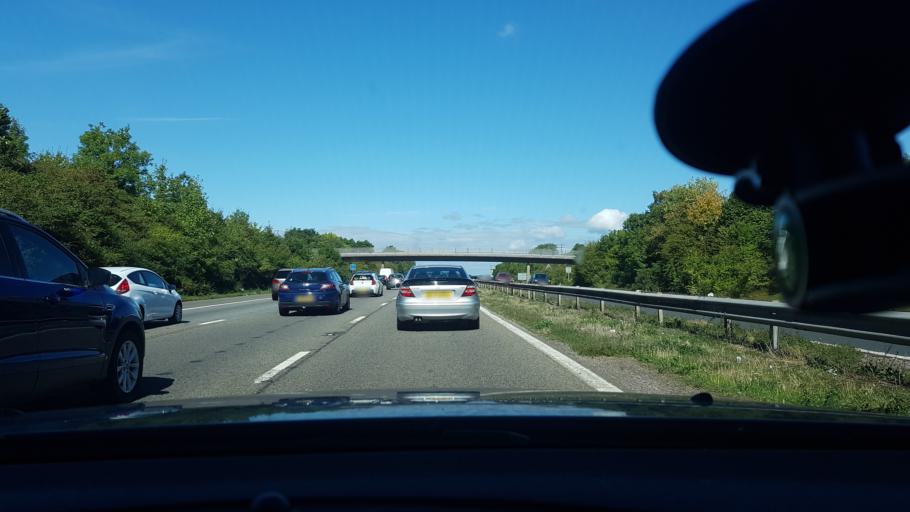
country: GB
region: England
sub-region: Somerset
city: Puriton
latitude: 51.1676
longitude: -2.9808
